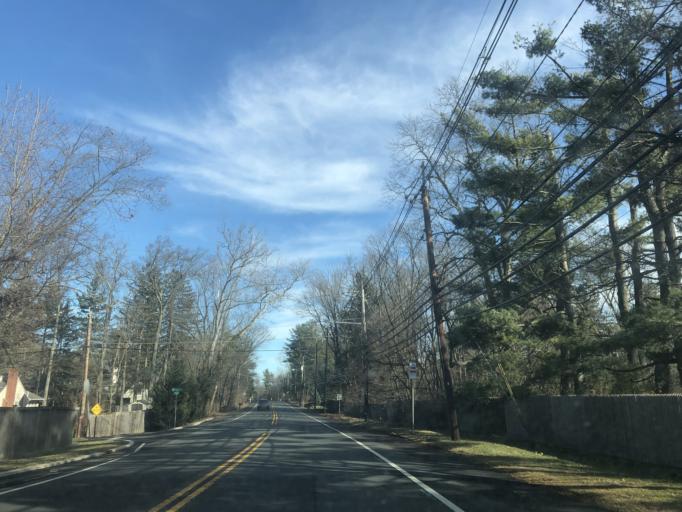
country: US
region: New Jersey
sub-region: Mercer County
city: Princeton
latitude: 40.3585
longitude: -74.6351
